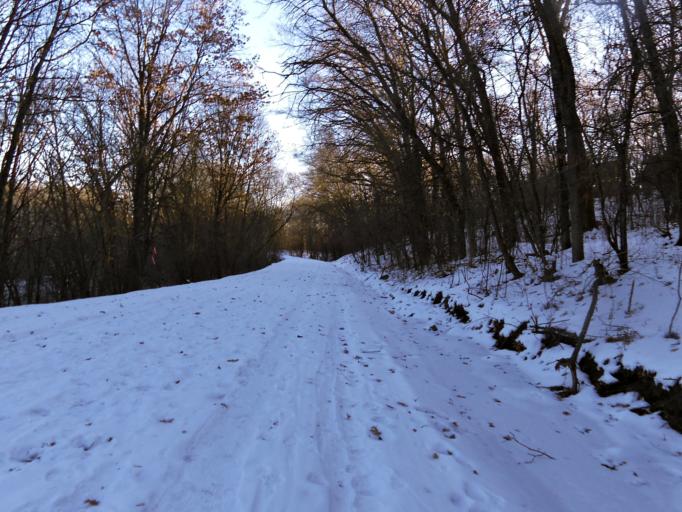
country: US
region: Minnesota
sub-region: Washington County
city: Grant
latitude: 45.0758
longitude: -92.8760
